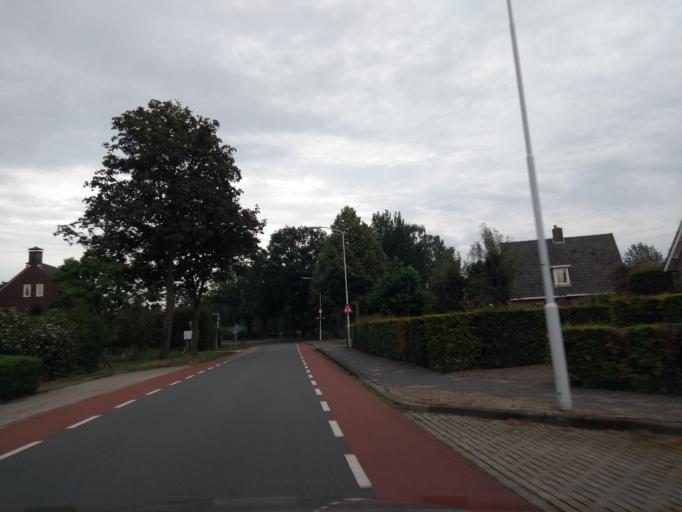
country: NL
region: Gelderland
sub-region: Oude IJsselstreek
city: Varsseveld
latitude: 51.9455
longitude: 6.4687
